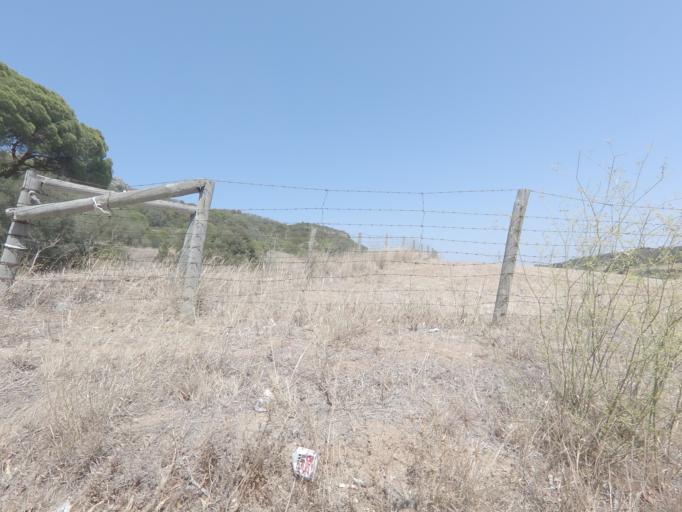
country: PT
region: Setubal
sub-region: Palmela
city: Quinta do Anjo
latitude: 38.5262
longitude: -8.9343
